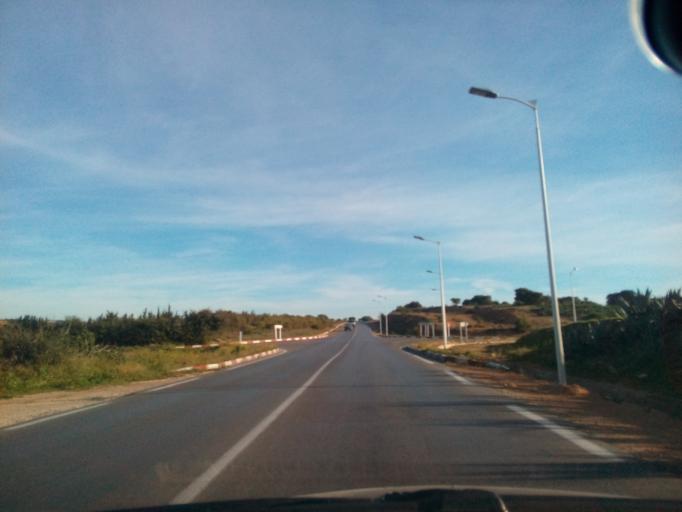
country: DZ
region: Mostaganem
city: Mostaganem
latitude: 35.8455
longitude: 0.1607
